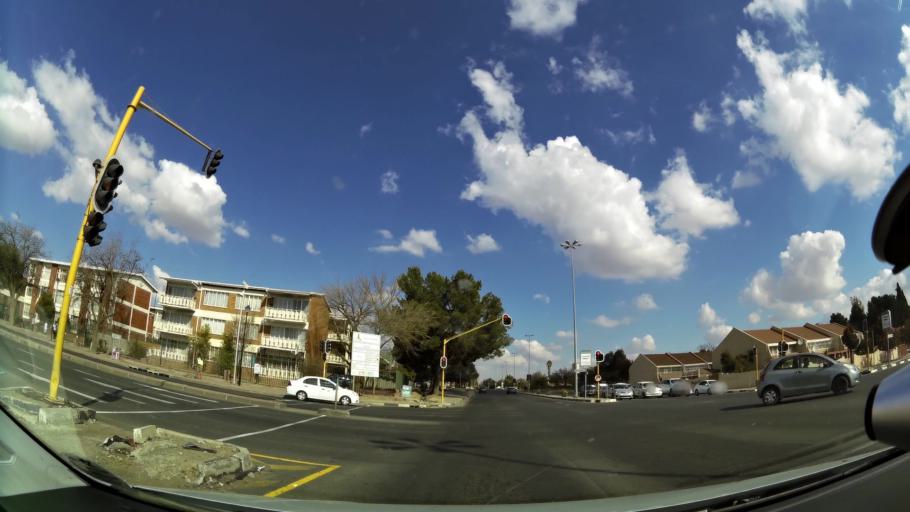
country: ZA
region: Orange Free State
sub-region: Mangaung Metropolitan Municipality
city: Bloemfontein
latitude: -29.1185
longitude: 26.2000
